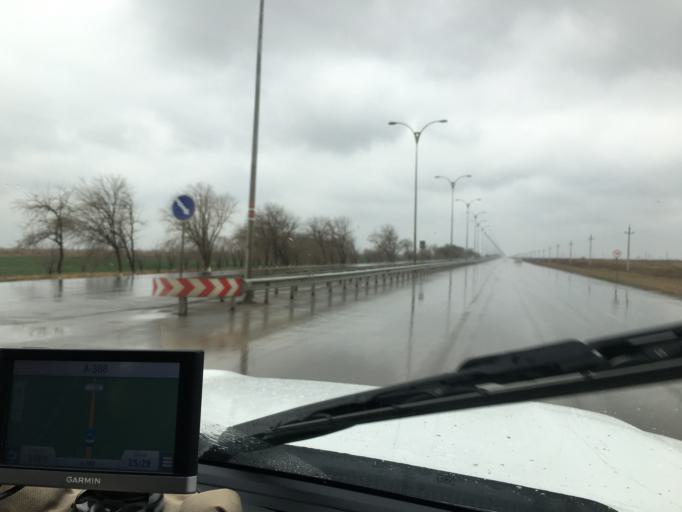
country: TM
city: Murgab
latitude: 37.5072
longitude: 61.9447
